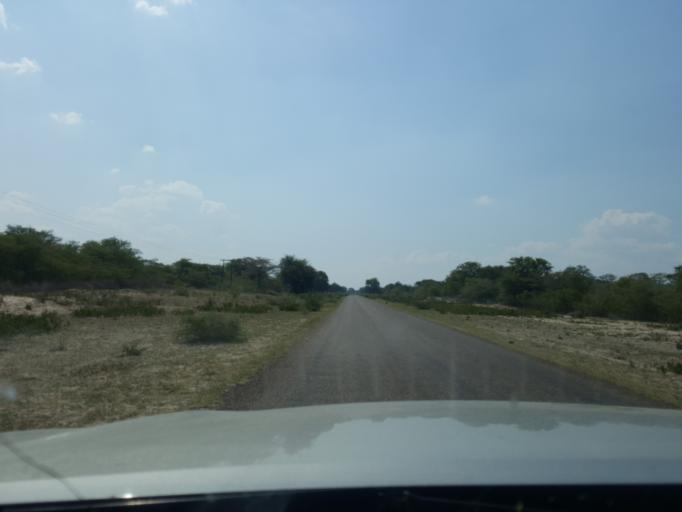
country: BW
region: North West
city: Shakawe
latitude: -18.8853
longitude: 22.2657
